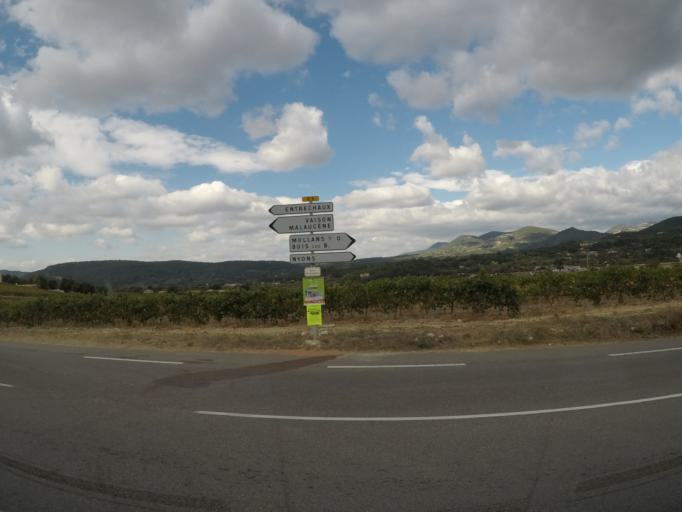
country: FR
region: Provence-Alpes-Cote d'Azur
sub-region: Departement du Vaucluse
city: Malaucene
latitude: 44.2303
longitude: 5.1779
